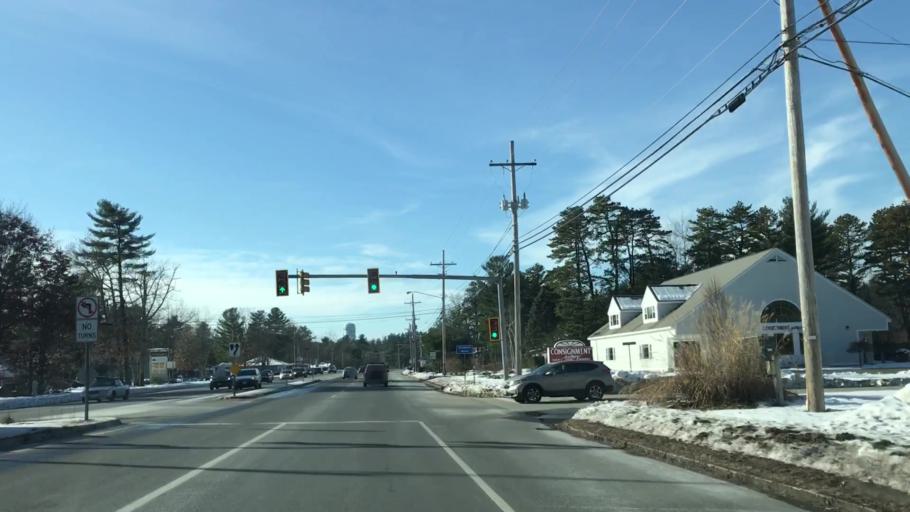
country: US
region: New Hampshire
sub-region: Hillsborough County
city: Hollis
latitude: 42.8115
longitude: -71.5836
